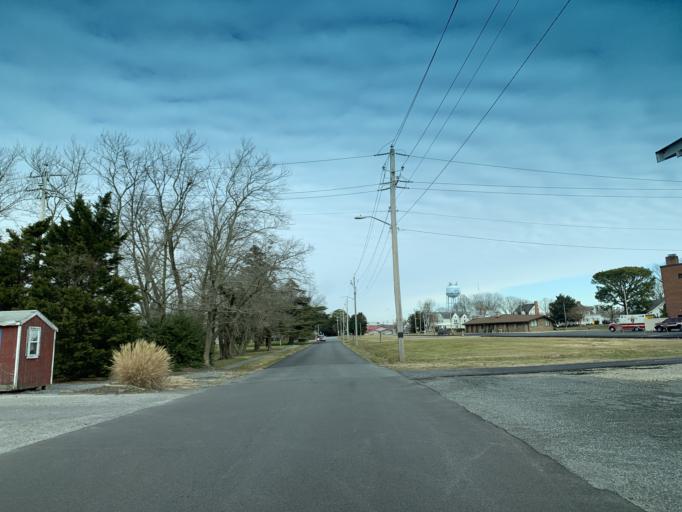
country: US
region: Maryland
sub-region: Worcester County
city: Berlin
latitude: 38.3281
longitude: -75.2218
